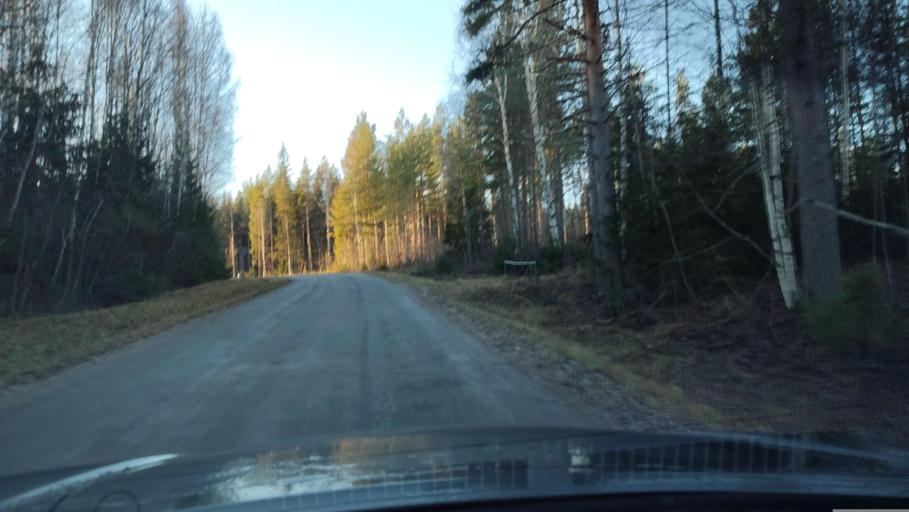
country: SE
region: Vaesterbotten
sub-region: Skelleftea Kommun
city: Viken
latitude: 64.7166
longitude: 20.9145
